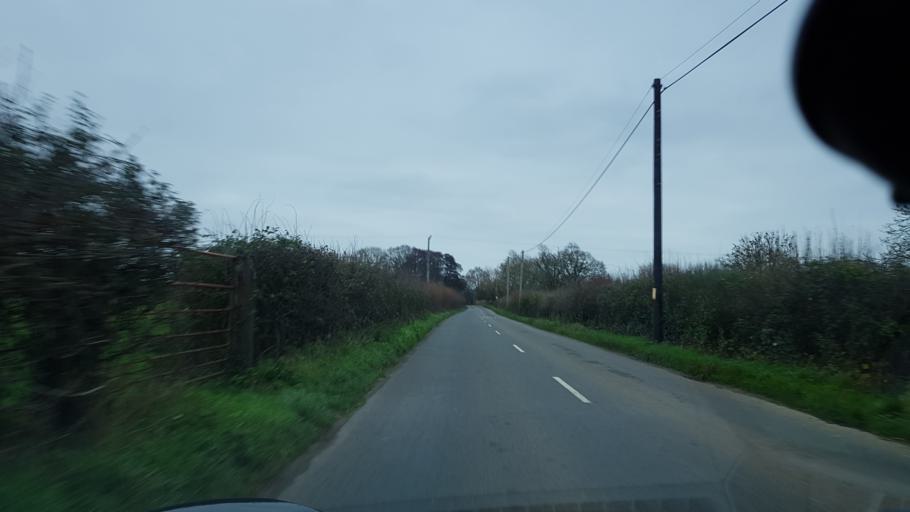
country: GB
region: England
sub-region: Somerset
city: Ilminster
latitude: 50.9485
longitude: -2.9239
